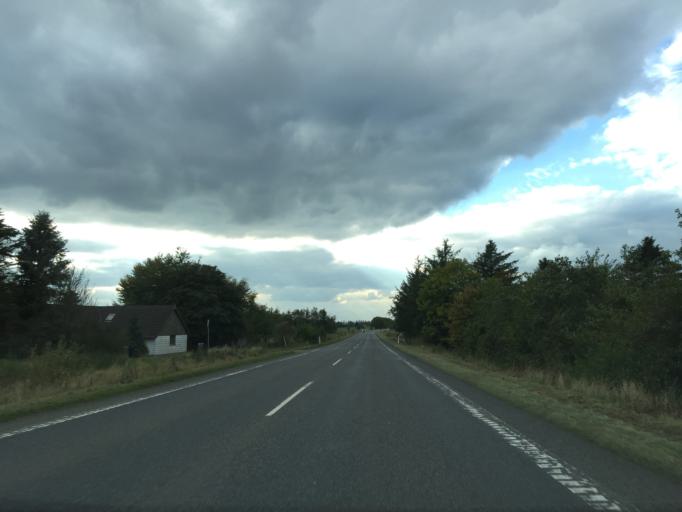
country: DK
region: Central Jutland
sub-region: Favrskov Kommune
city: Ulstrup
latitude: 56.3224
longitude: 9.8043
